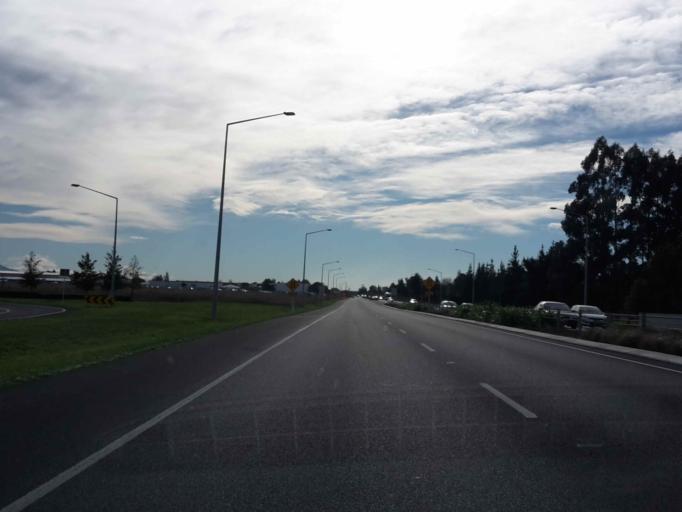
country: NZ
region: Canterbury
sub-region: Selwyn District
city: Prebbleton
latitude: -43.5023
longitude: 172.5444
